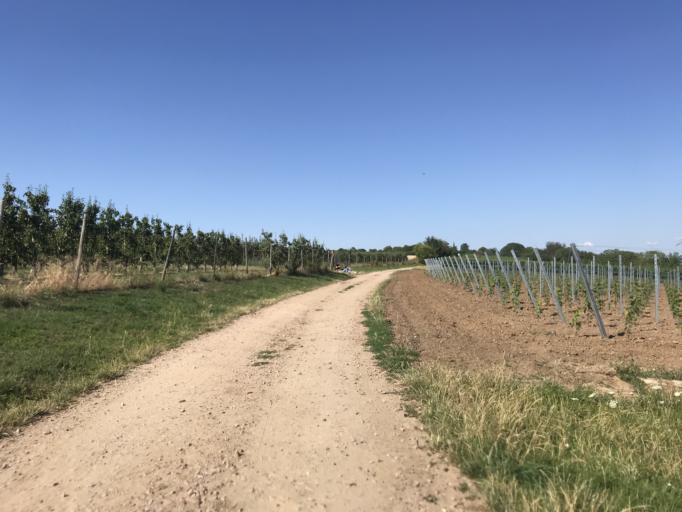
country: DE
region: Rheinland-Pfalz
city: Ockenheim
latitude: 49.9387
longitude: 7.9947
